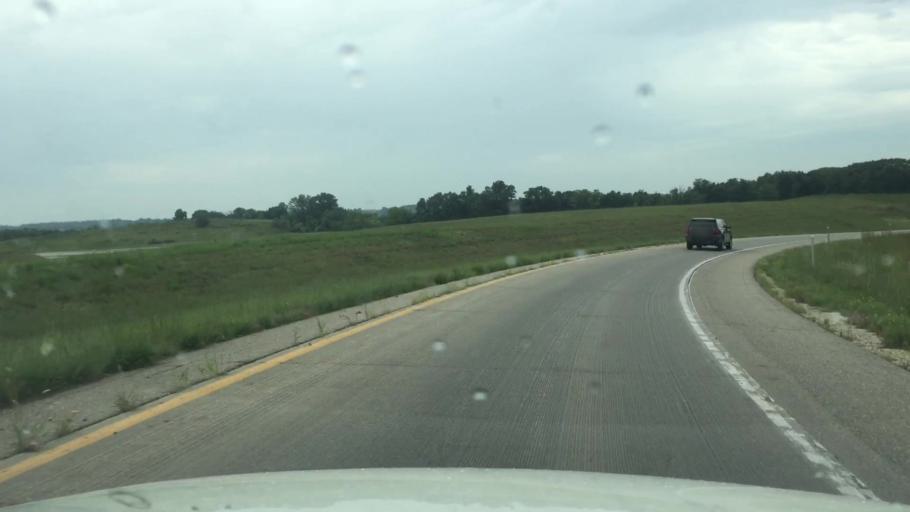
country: US
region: Iowa
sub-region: Warren County
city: Carlisle
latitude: 41.5080
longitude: -93.5748
